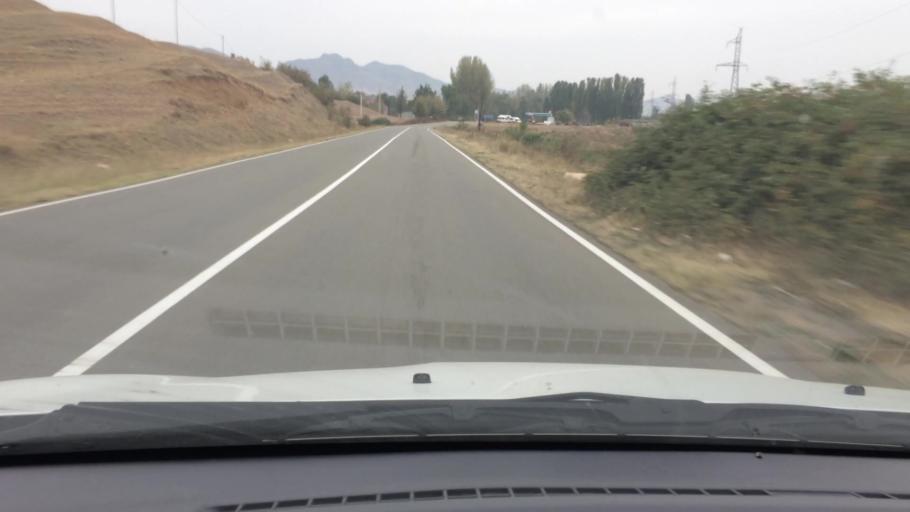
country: AM
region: Tavush
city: Bagratashen
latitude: 41.2888
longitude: 44.7888
